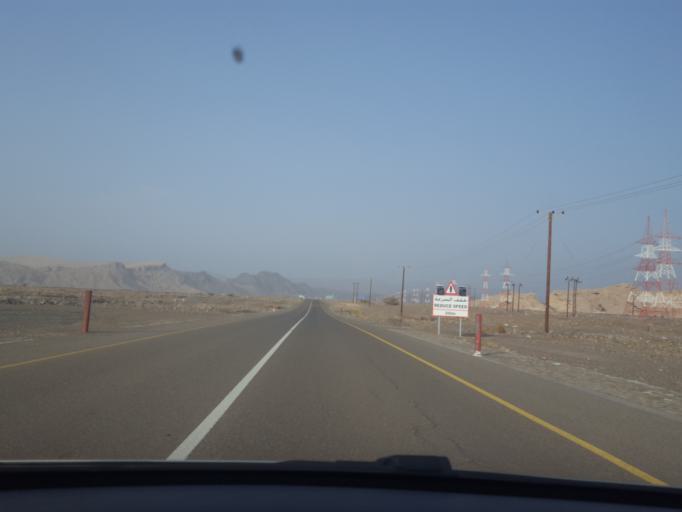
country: AE
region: Abu Dhabi
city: Al Ain
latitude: 24.0379
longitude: 56.0162
